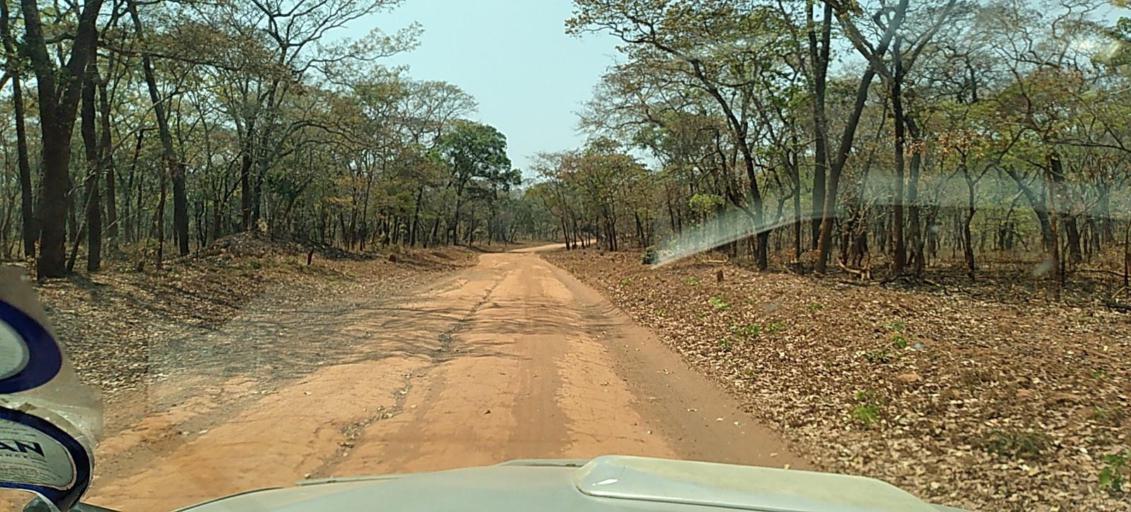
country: ZM
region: North-Western
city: Kasempa
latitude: -13.5485
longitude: 26.0586
